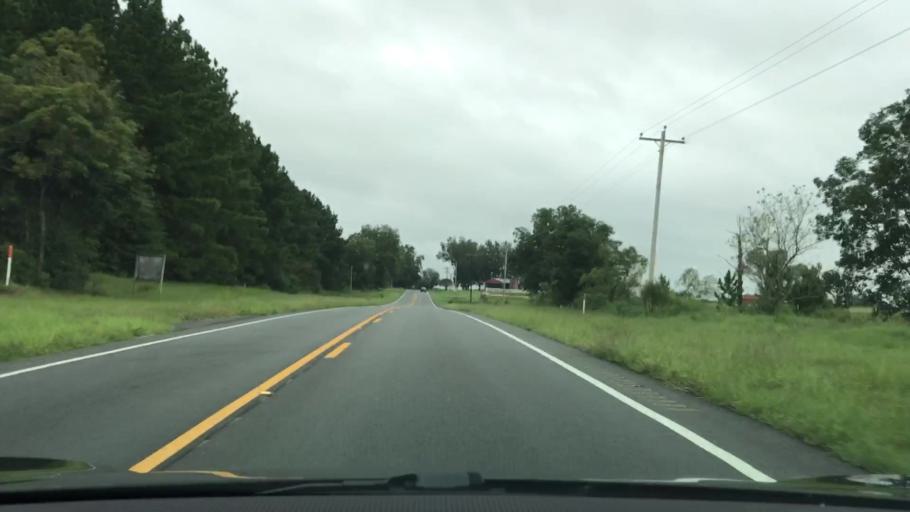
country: US
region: Alabama
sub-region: Covington County
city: Opp
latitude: 31.2322
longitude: -86.1618
